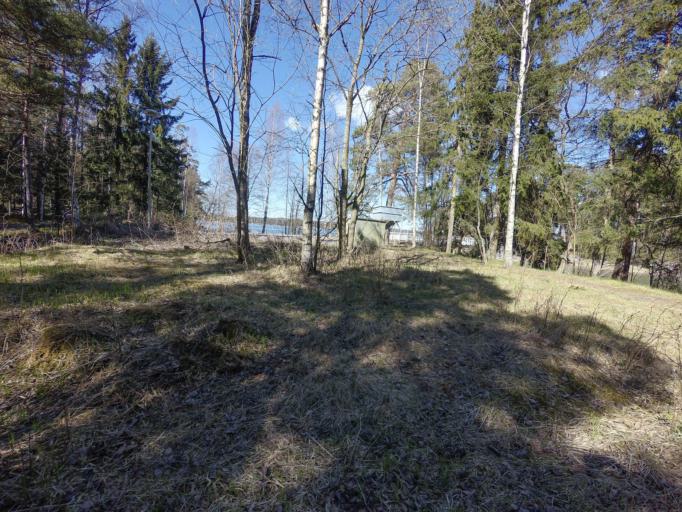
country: FI
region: Uusimaa
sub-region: Helsinki
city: Vantaa
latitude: 60.1693
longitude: 25.0677
